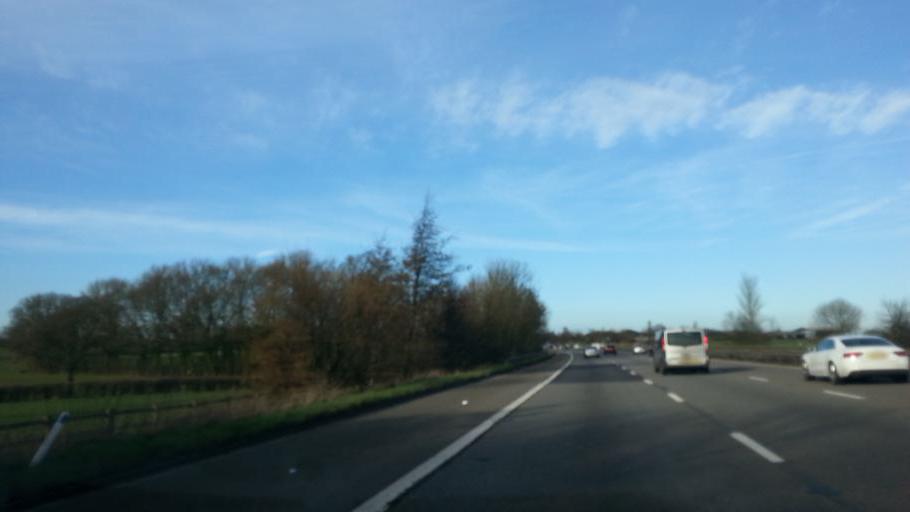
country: GB
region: England
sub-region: Warwickshire
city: Bedworth
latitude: 52.4669
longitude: -1.4083
